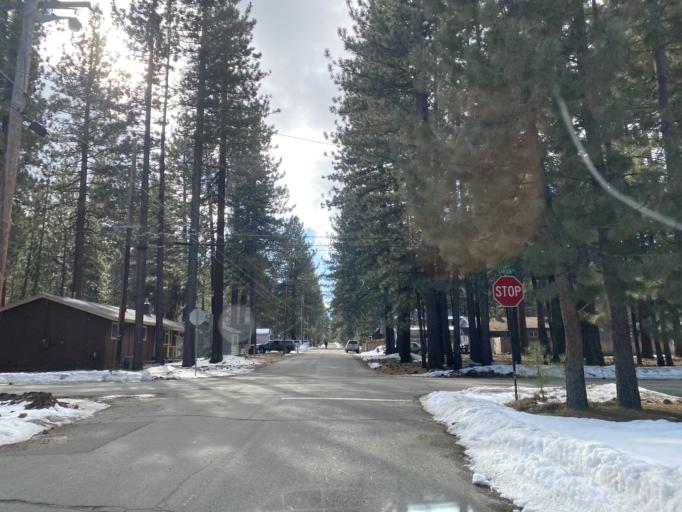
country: US
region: California
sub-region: El Dorado County
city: South Lake Tahoe
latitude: 38.9212
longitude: -119.9770
